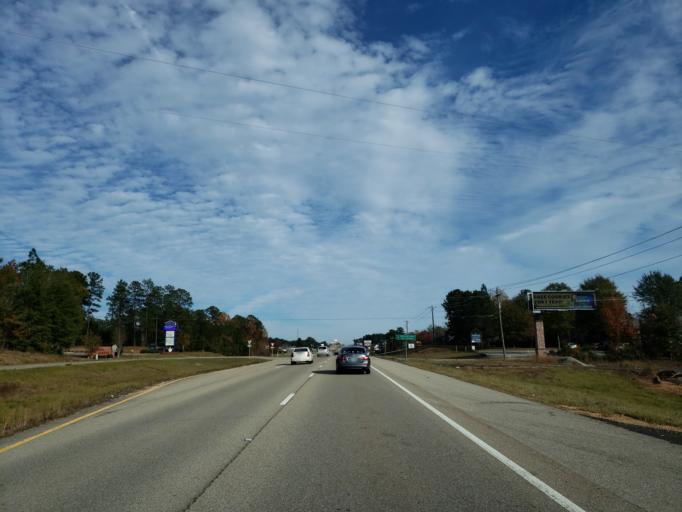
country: US
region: Mississippi
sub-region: Lamar County
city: West Hattiesburg
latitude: 31.3158
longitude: -89.4371
